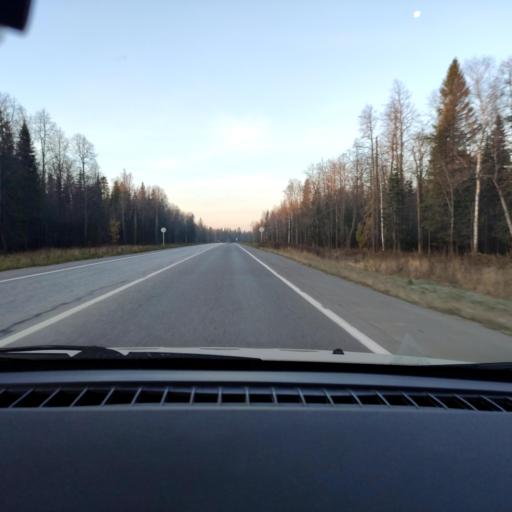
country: RU
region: Perm
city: Novyye Lyady
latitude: 58.0306
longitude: 56.5231
